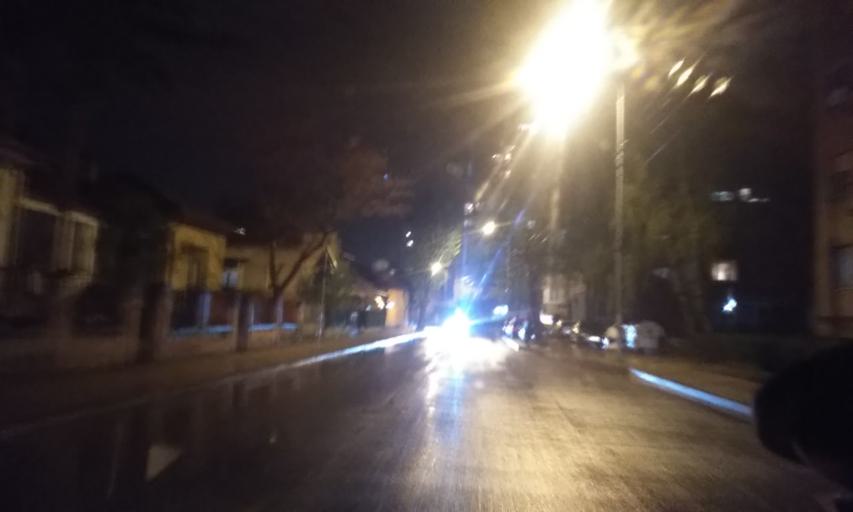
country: RS
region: Central Serbia
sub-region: Nisavski Okrug
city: Nis
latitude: 43.3152
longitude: 21.8997
